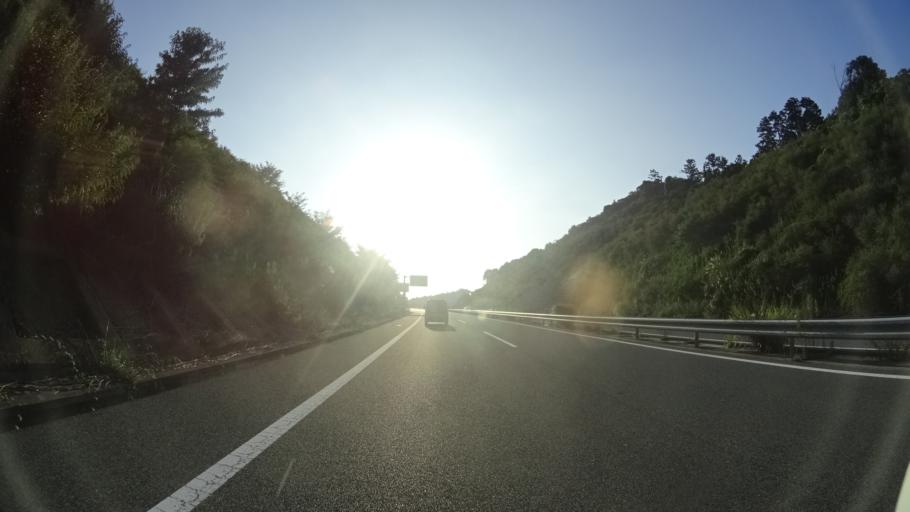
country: JP
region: Yamaguchi
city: Hagi
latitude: 34.3891
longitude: 131.3289
